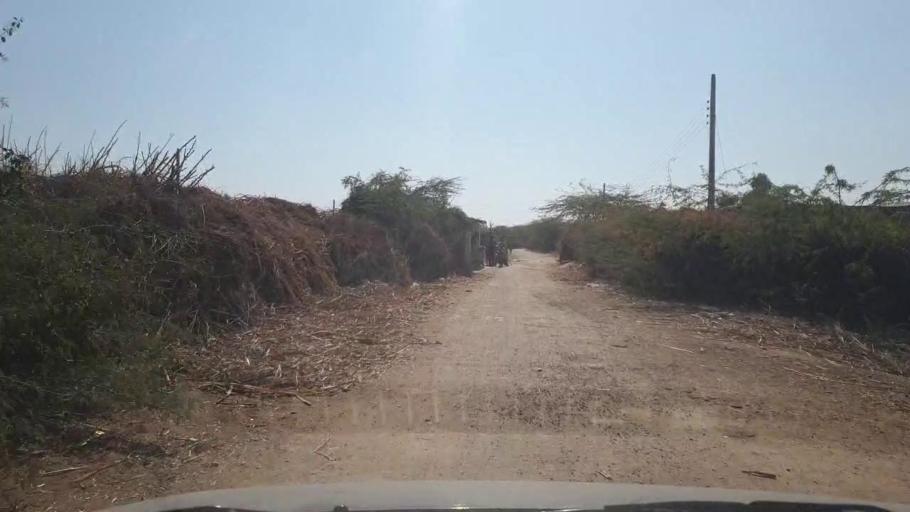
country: PK
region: Sindh
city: Samaro
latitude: 25.2707
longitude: 69.2671
